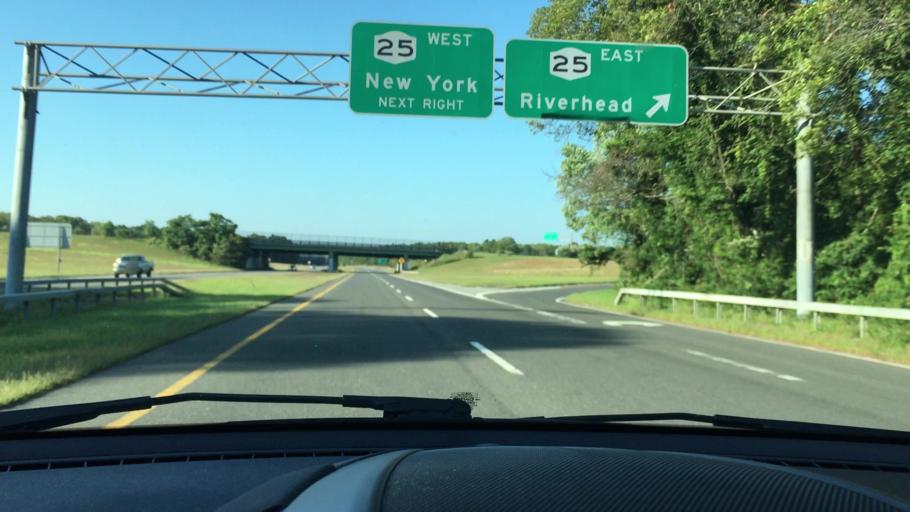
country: US
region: New York
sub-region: Suffolk County
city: Ridge
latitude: 40.8937
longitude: -72.8837
